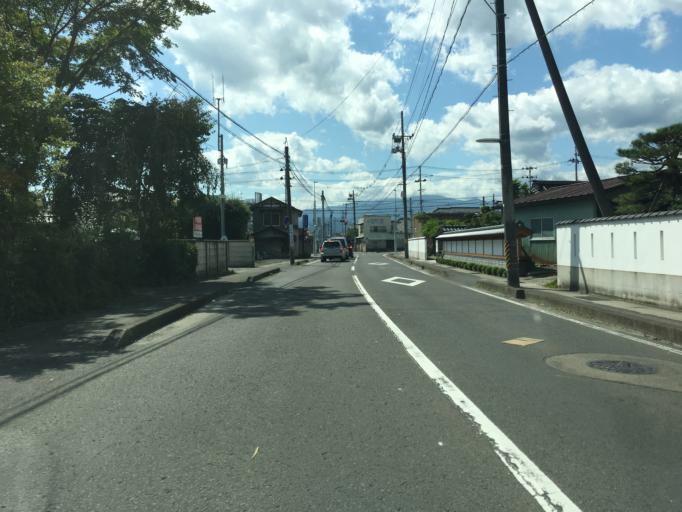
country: JP
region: Fukushima
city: Fukushima-shi
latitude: 37.7731
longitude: 140.4239
